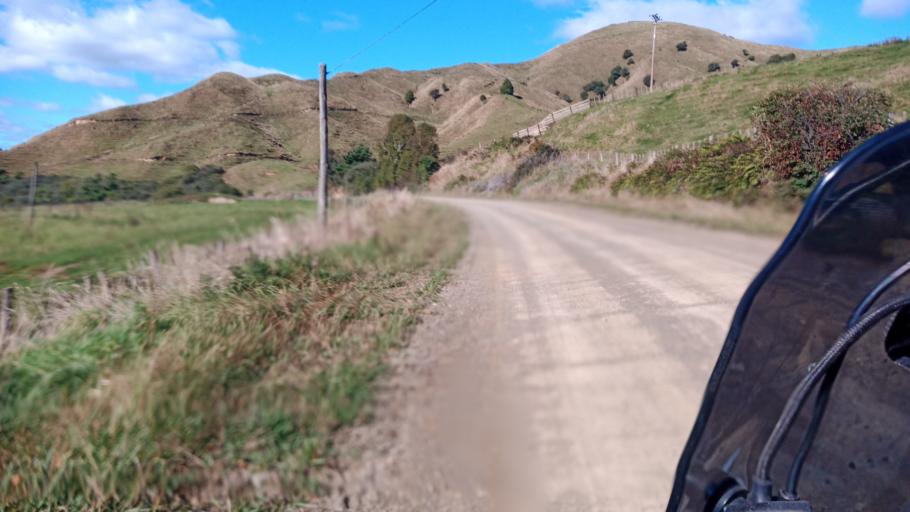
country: NZ
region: Bay of Plenty
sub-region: Opotiki District
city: Opotiki
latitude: -38.2563
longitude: 177.5706
